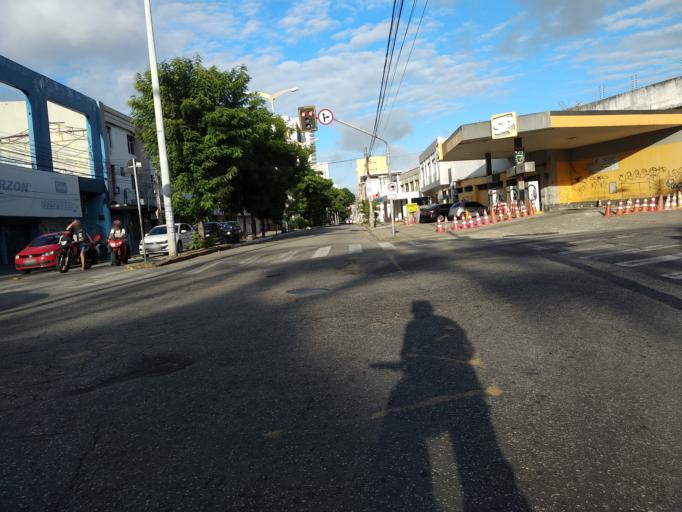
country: BR
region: Ceara
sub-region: Fortaleza
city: Fortaleza
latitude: -3.7333
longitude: -38.5250
